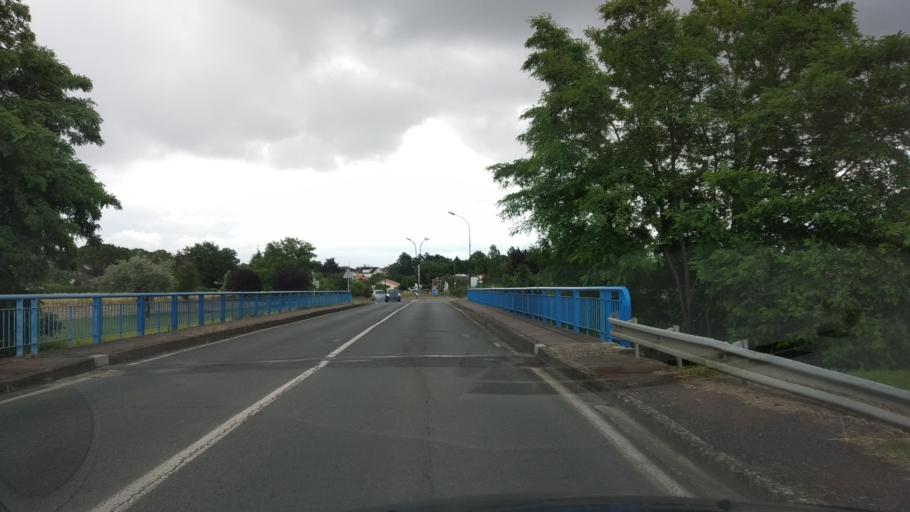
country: FR
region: Poitou-Charentes
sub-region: Departement de la Vienne
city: Biard
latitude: 46.5624
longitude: 0.3021
